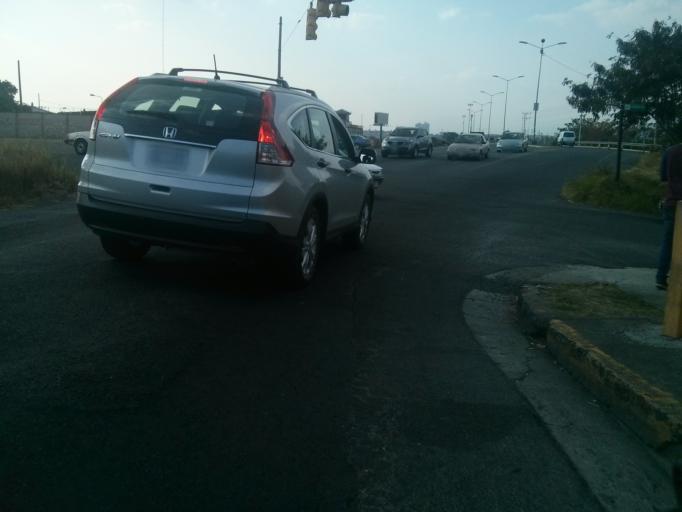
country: CR
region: San Jose
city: San Jose
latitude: 9.9103
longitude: -84.0728
